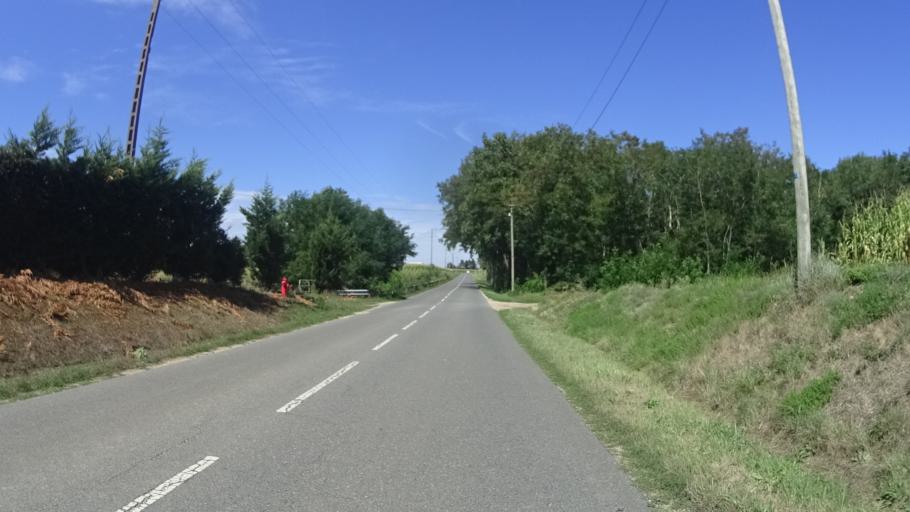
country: FR
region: Centre
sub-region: Departement du Loiret
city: Briare
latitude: 47.6166
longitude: 2.7548
